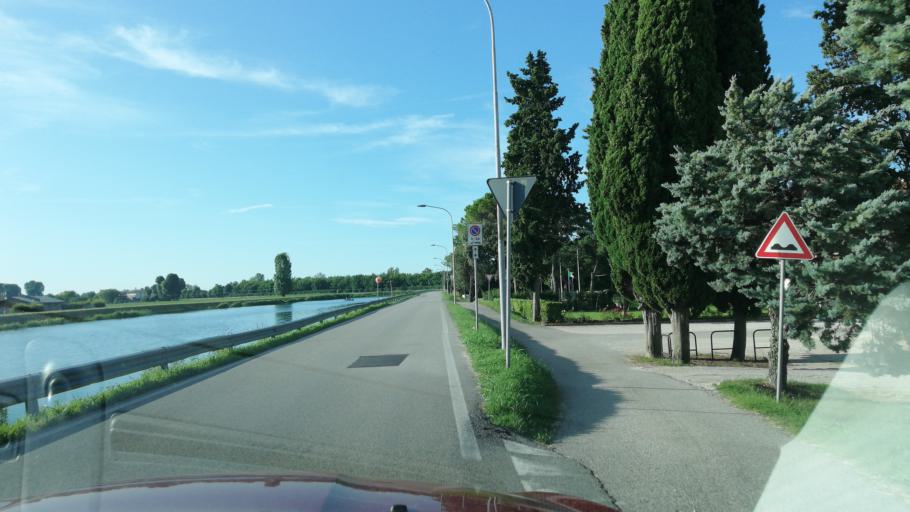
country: IT
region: Veneto
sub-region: Provincia di Venezia
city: San Giorgio di Livenza
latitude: 45.6445
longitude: 12.7899
